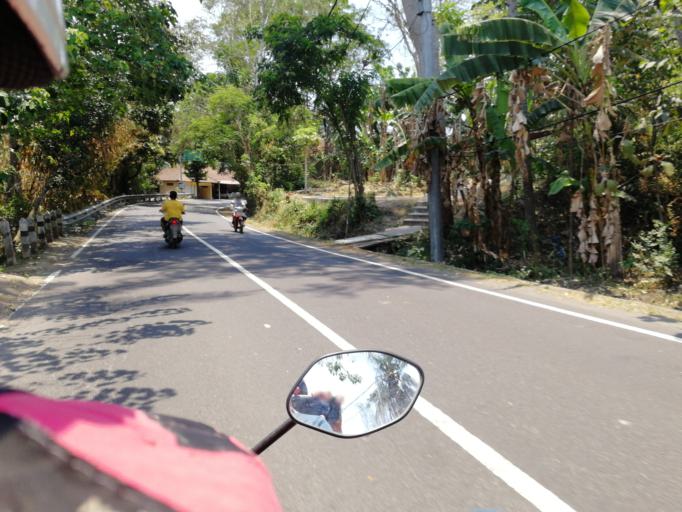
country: ID
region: Bali
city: Padangbai
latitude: -8.5214
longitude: 115.4993
